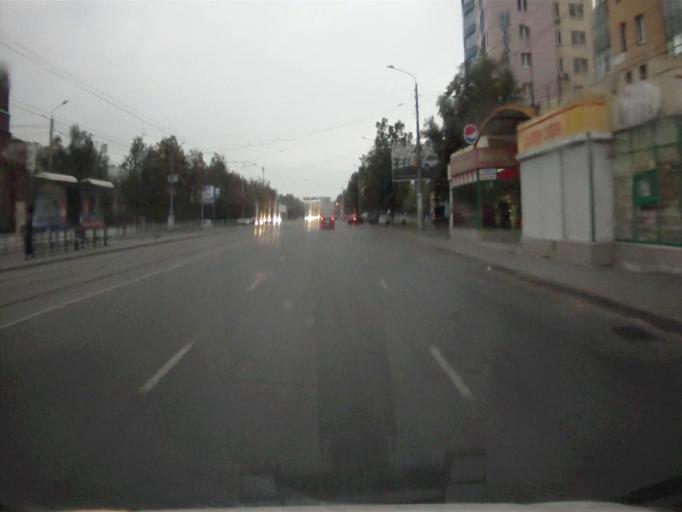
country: RU
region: Chelyabinsk
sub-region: Gorod Chelyabinsk
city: Chelyabinsk
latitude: 55.1737
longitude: 61.4000
